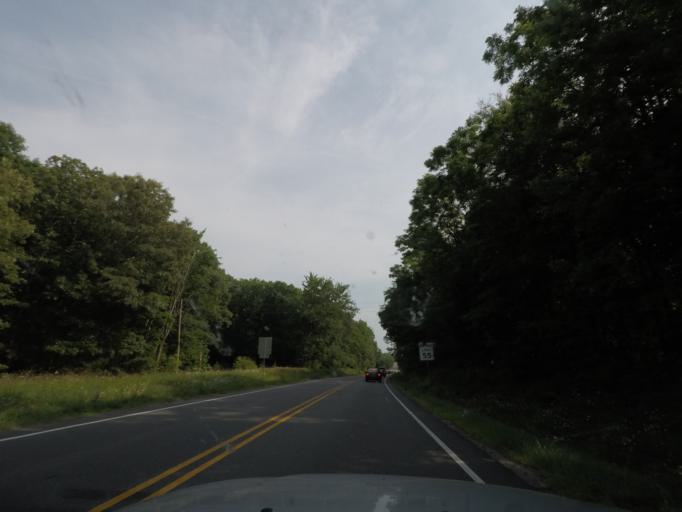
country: US
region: Virginia
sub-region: Prince Edward County
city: Hampden Sydney
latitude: 37.2429
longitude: -78.4436
